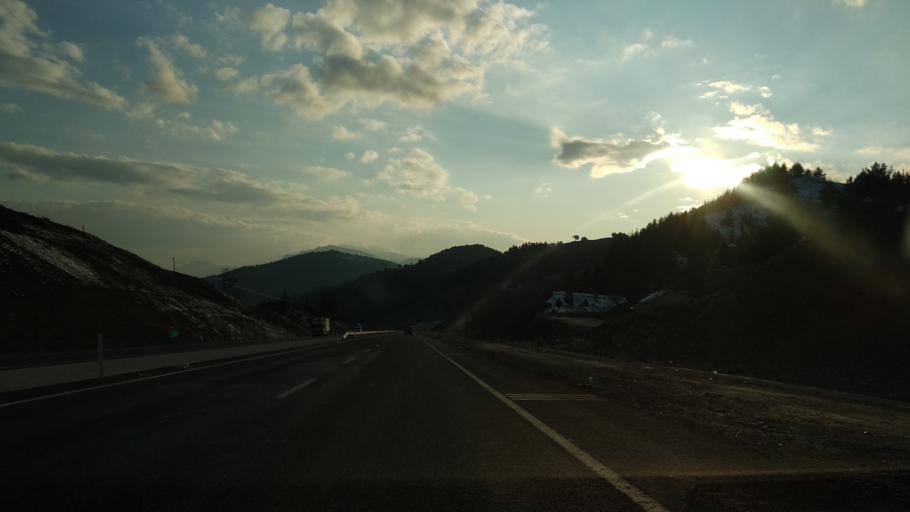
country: TR
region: Kahramanmaras
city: Yenicekale
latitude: 37.7124
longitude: 36.6933
